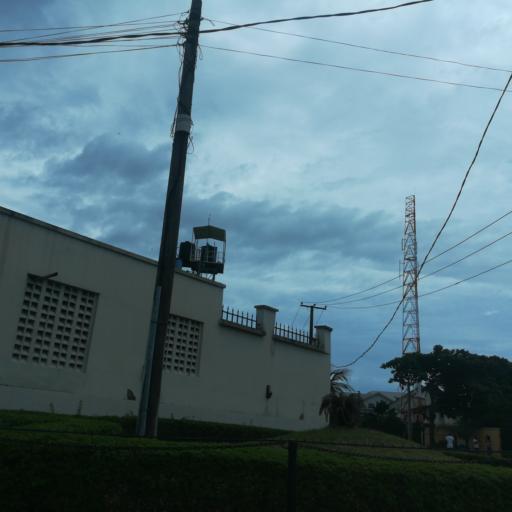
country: NG
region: Lagos
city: Ikoyi
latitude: 6.4463
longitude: 3.4650
